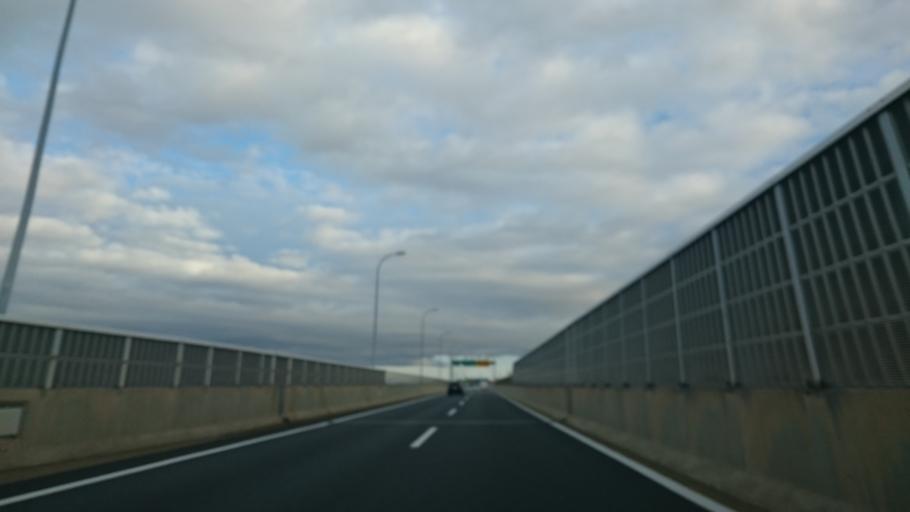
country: JP
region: Aichi
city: Komaki
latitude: 35.2488
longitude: 136.9081
